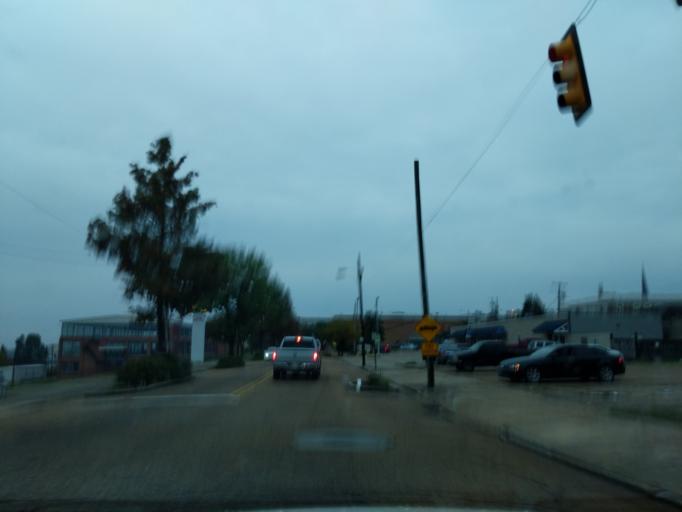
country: US
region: Mississippi
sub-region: Warren County
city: Vicksburg
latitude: 32.3450
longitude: -90.8833
